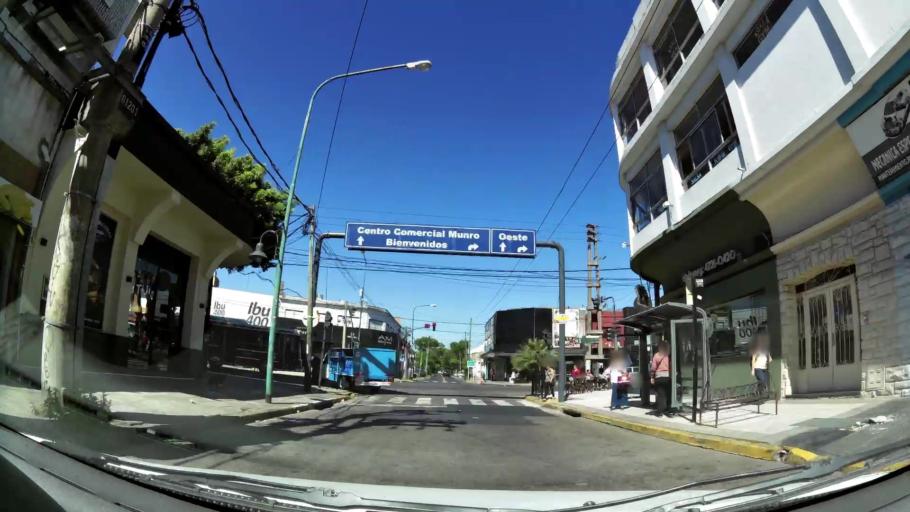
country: AR
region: Buenos Aires
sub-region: Partido de Vicente Lopez
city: Olivos
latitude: -34.5296
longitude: -58.5159
